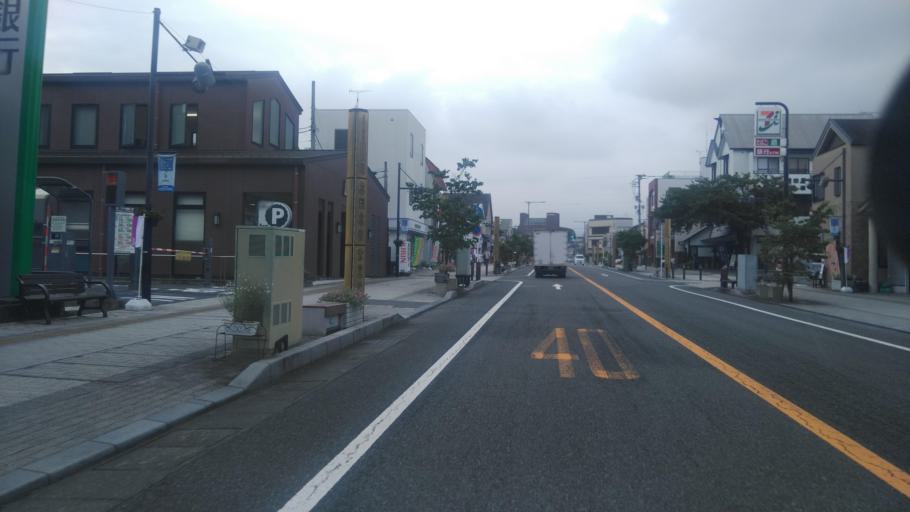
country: JP
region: Shizuoka
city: Fujinomiya
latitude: 35.2228
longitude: 138.6147
